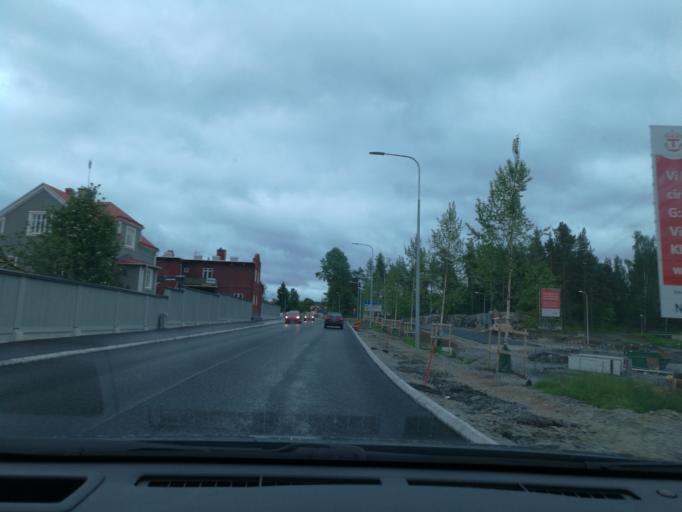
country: SE
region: Dalarna
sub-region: Ludvika Kommun
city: Ludvika
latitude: 60.1525
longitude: 15.1947
